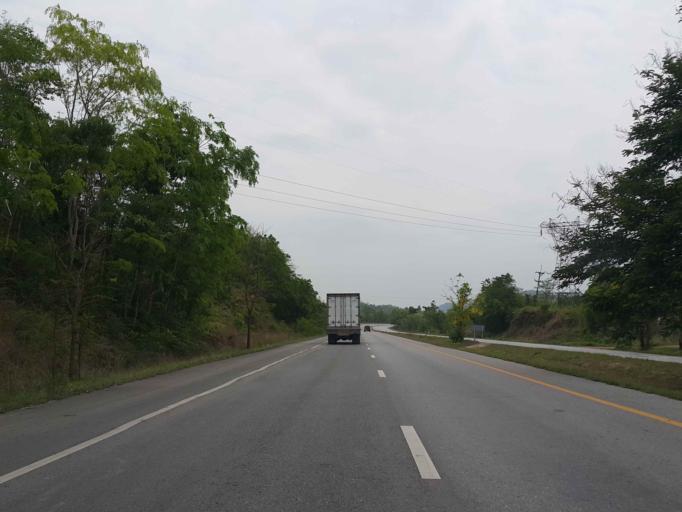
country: TH
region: Lampang
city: Sop Prap
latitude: 17.8580
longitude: 99.3073
